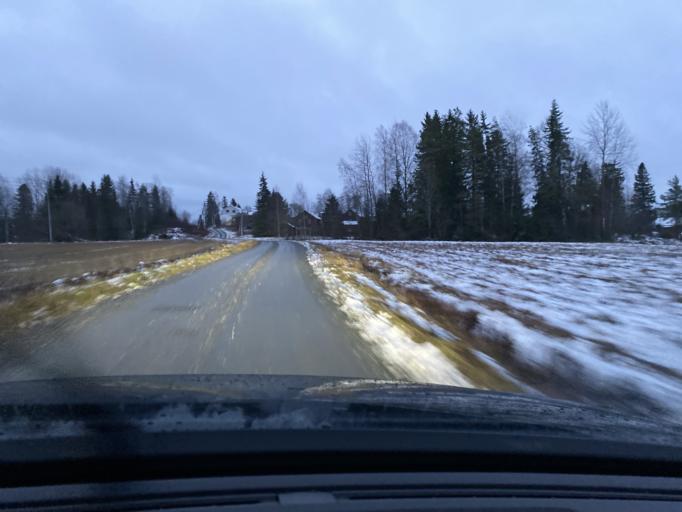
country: FI
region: Pirkanmaa
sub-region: Lounais-Pirkanmaa
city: Punkalaidun
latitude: 61.1198
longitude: 23.0440
